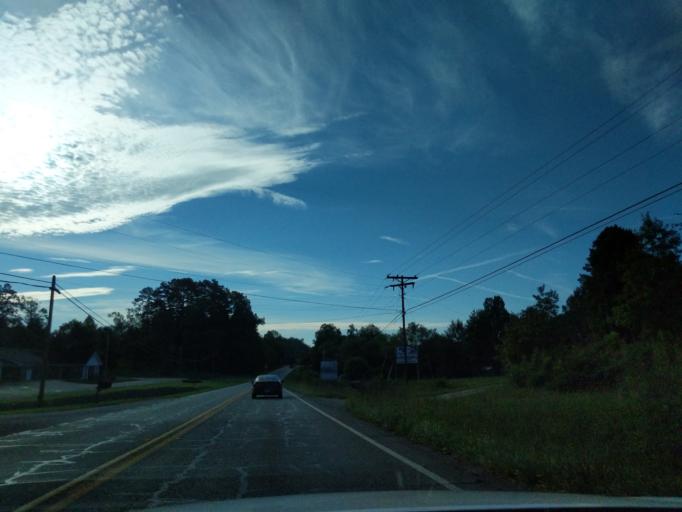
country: US
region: Georgia
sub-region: Fannin County
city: Blue Ridge
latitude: 34.8937
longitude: -84.3537
